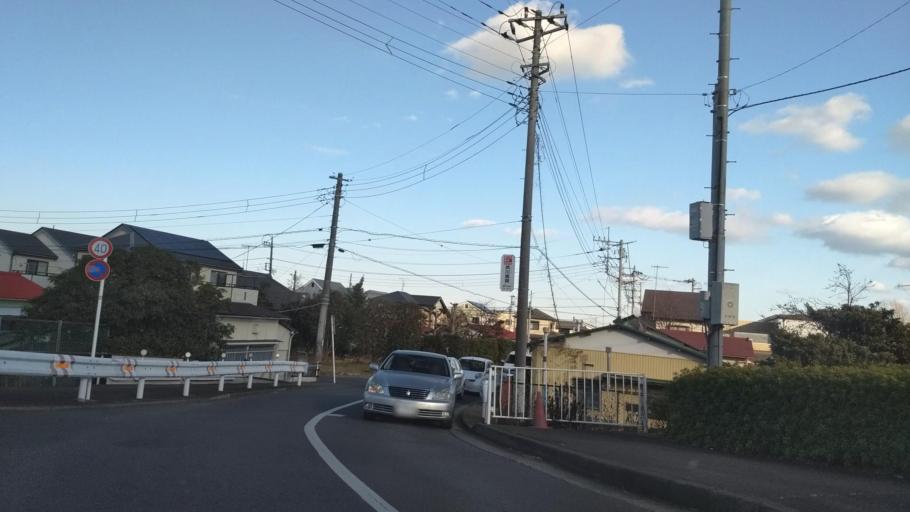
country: JP
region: Kanagawa
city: Isehara
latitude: 35.3569
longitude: 139.3050
